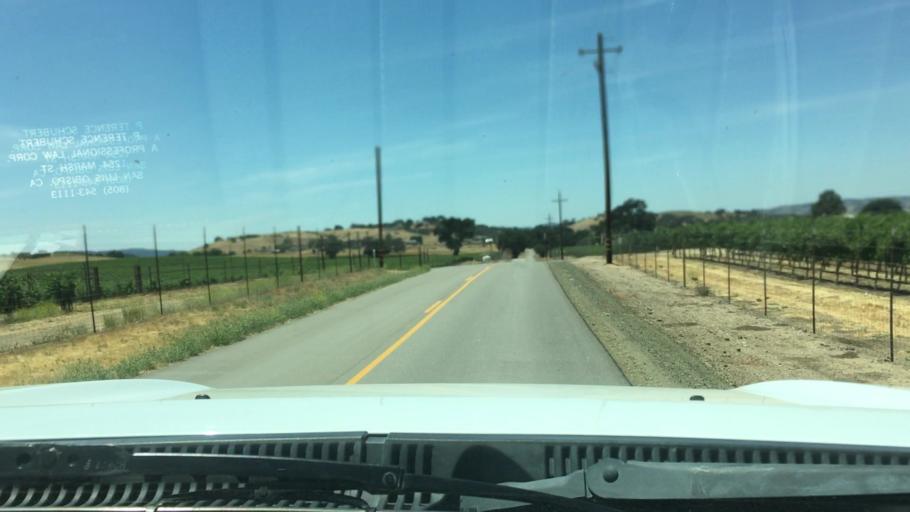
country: US
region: California
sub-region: San Luis Obispo County
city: Paso Robles
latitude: 35.5753
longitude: -120.6227
